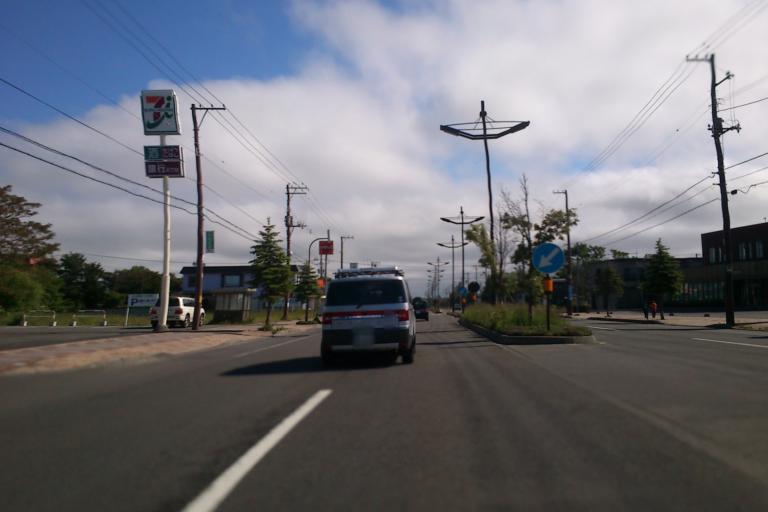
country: JP
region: Hokkaido
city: Ishikari
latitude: 43.1736
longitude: 141.3156
